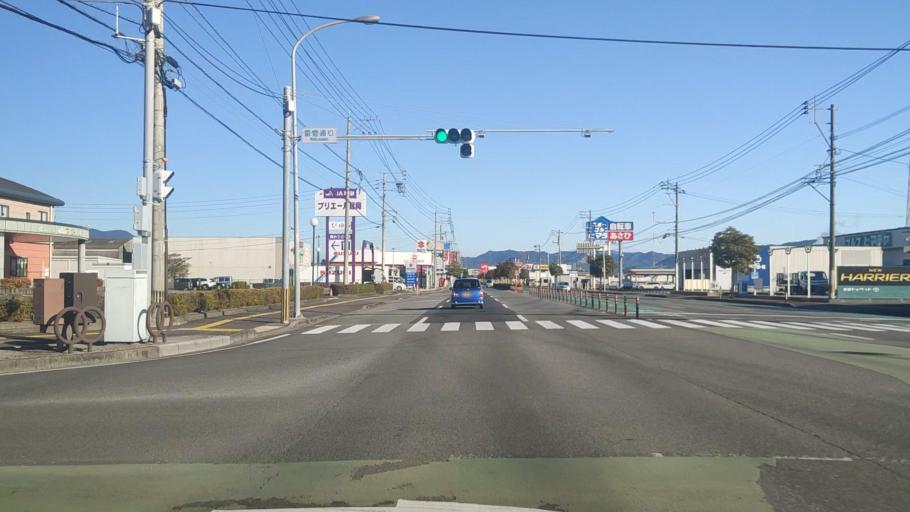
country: JP
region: Miyazaki
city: Nobeoka
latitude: 32.5627
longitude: 131.6815
